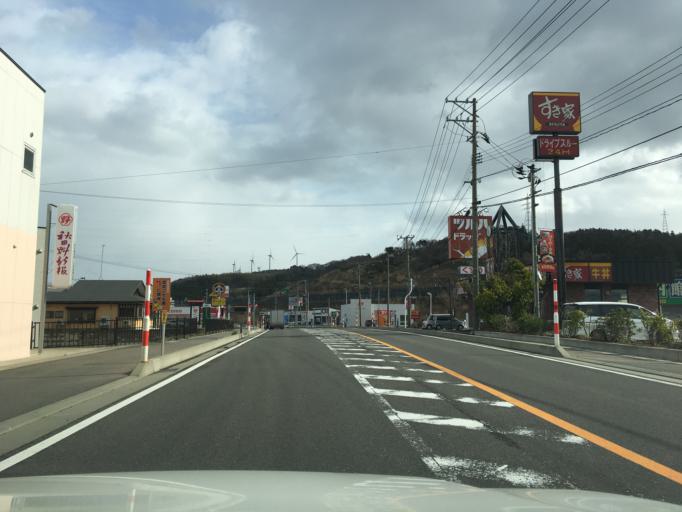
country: JP
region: Yamagata
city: Yuza
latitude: 39.2894
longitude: 139.9722
